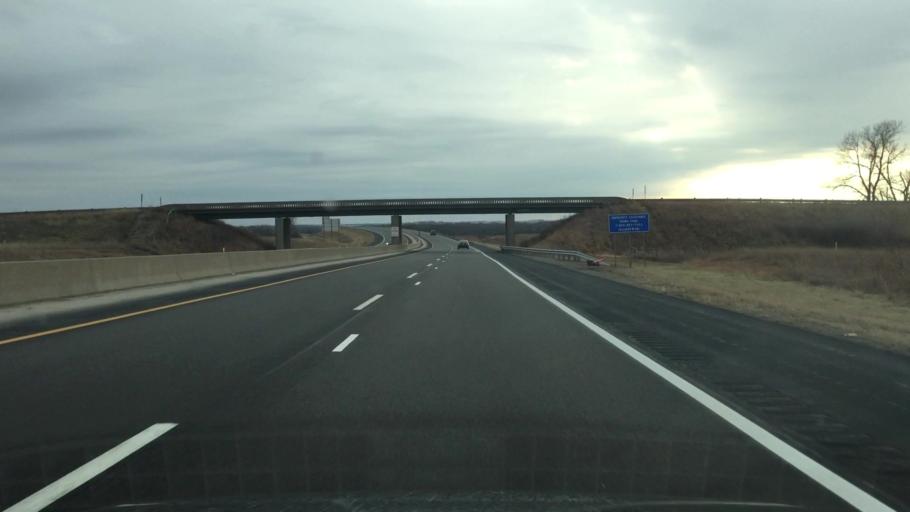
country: US
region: Kansas
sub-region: Osage County
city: Osage City
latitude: 38.6361
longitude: -96.0407
